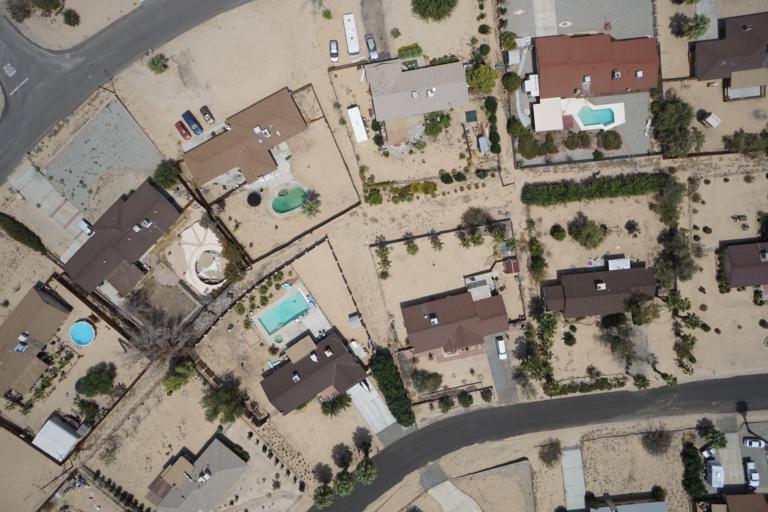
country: US
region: California
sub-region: San Bernardino County
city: Twentynine Palms
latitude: 34.1552
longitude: -116.0470
